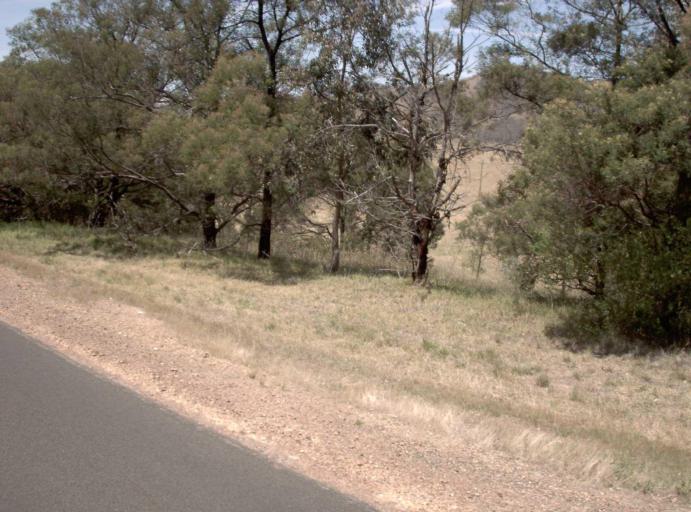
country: AU
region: Victoria
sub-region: East Gippsland
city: Bairnsdale
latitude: -37.1719
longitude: 147.6930
